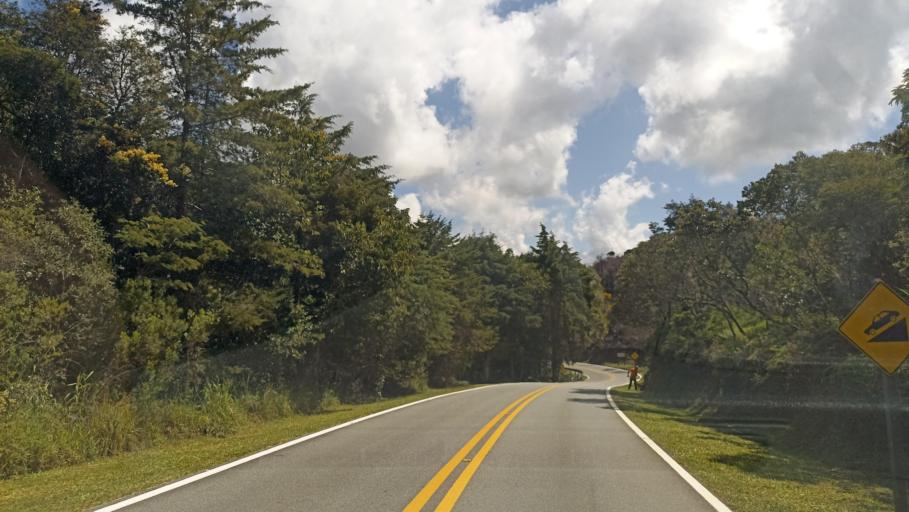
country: BR
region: Sao Paulo
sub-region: Cunha
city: Cunha
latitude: -23.1383
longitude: -44.9011
